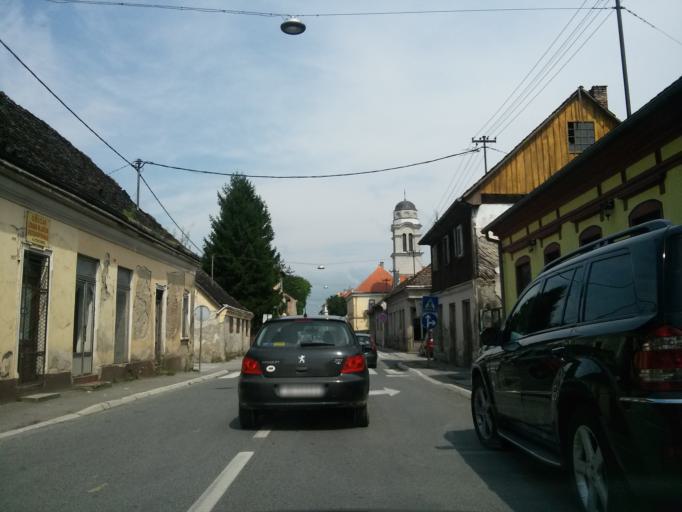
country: HR
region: Sisacko-Moslavacka
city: Glina
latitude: 45.3391
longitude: 16.0916
